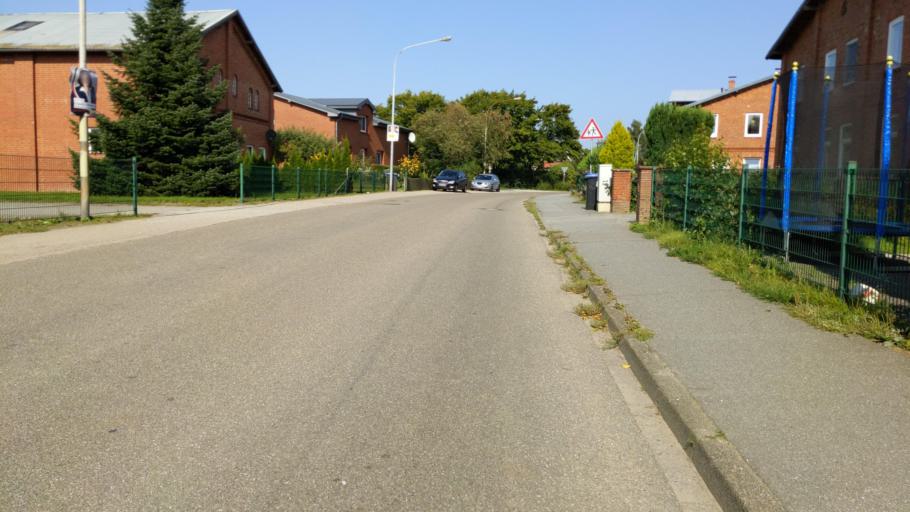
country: DE
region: Schleswig-Holstein
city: Stockelsdorf
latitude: 53.8813
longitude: 10.6230
